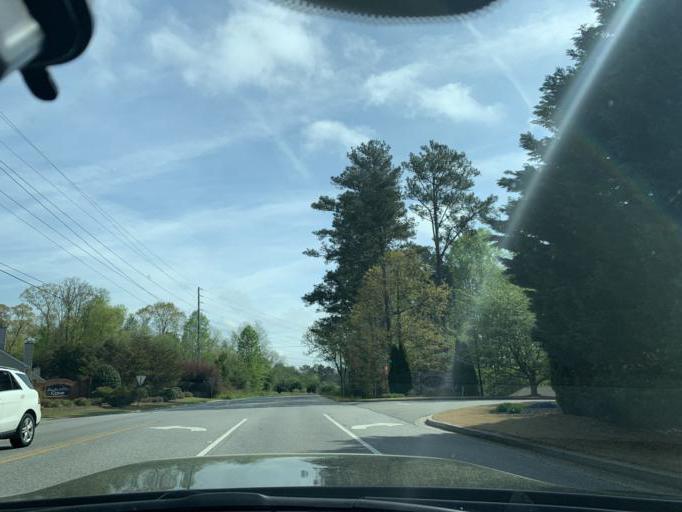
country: US
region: Georgia
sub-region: Forsyth County
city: Cumming
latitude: 34.2478
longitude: -84.0806
